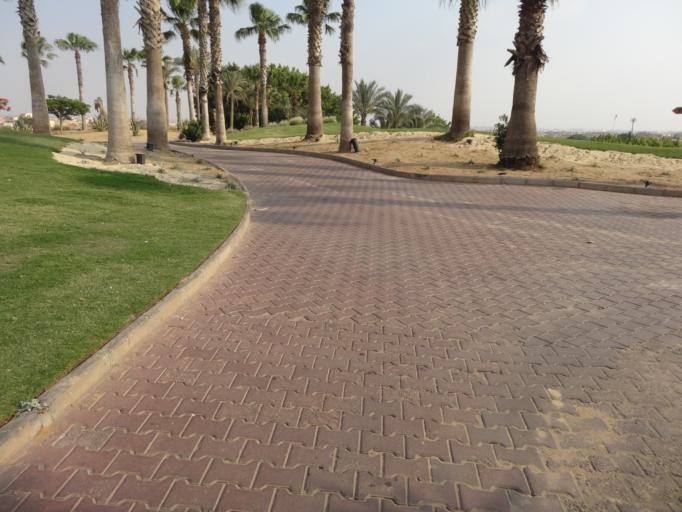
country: EG
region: Muhafazat al Qalyubiyah
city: Al Khankah
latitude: 30.0692
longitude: 31.4347
